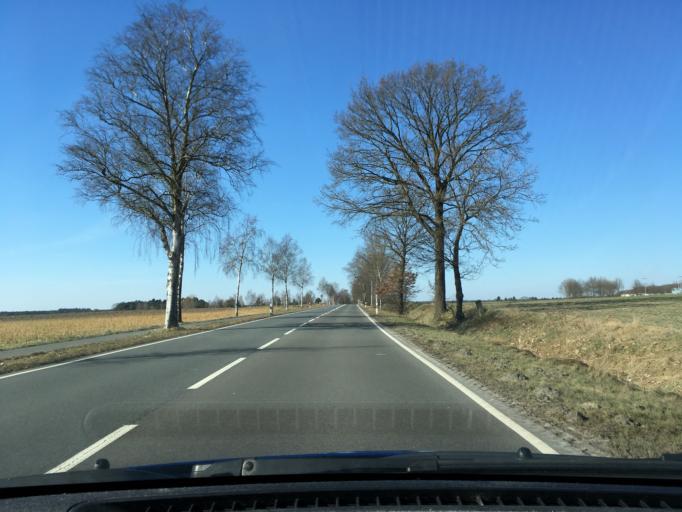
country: DE
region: Lower Saxony
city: Hemslingen
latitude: 53.0875
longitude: 9.5915
